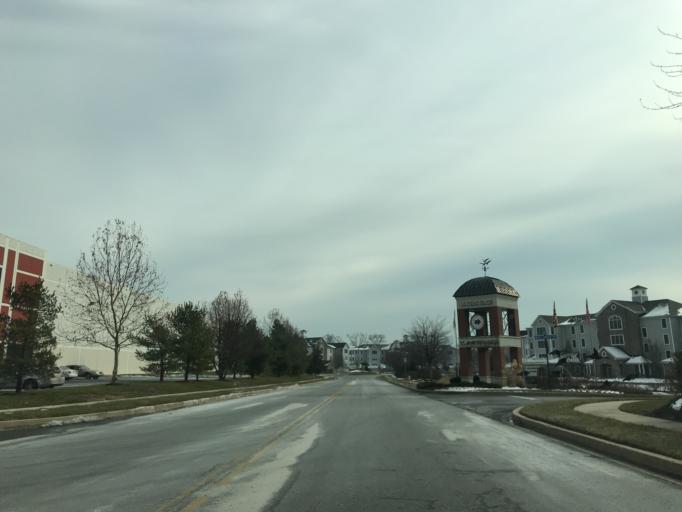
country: US
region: Maryland
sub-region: Harford County
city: Riverside
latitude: 39.4684
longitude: -76.2351
